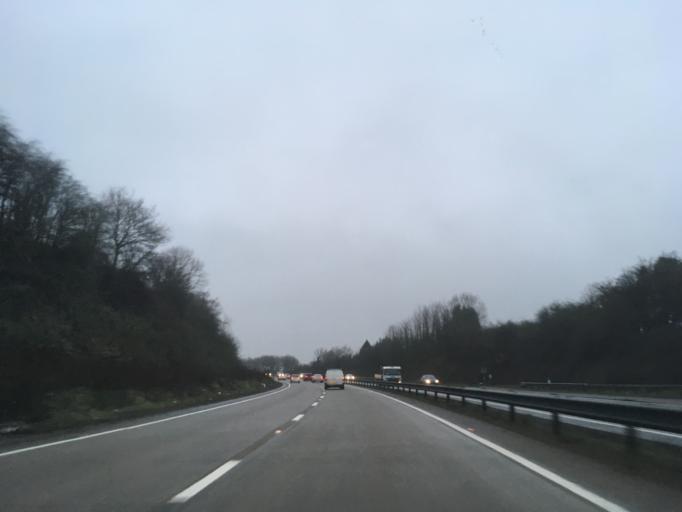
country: GB
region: Wales
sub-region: Cardiff
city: Pentyrch
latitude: 51.4975
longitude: -3.2956
